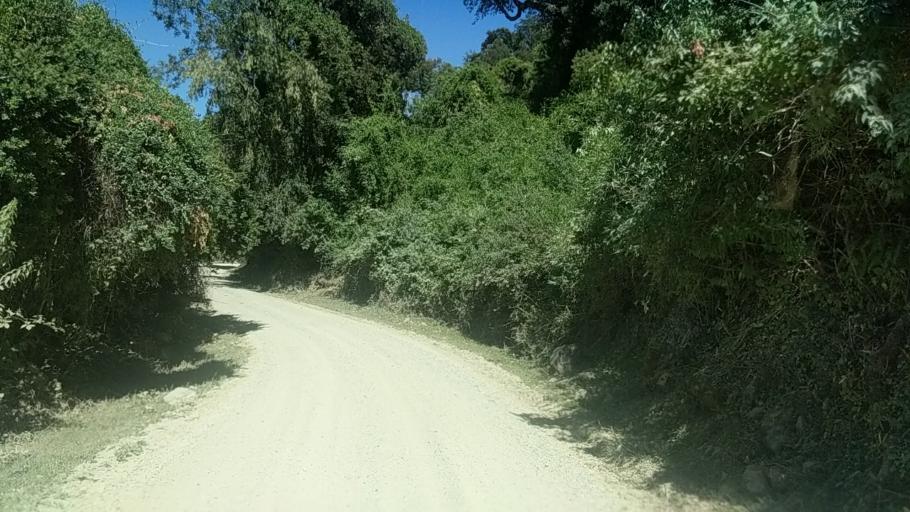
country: CL
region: Araucania
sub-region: Provincia de Cautin
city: Pucon
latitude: -39.0619
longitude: -71.7057
